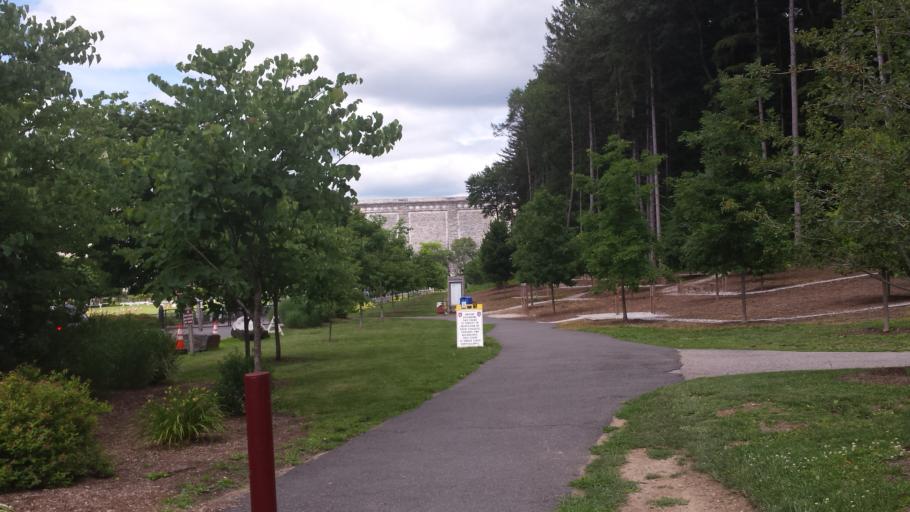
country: US
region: New York
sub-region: Westchester County
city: Valhalla
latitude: 41.0701
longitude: -73.7677
